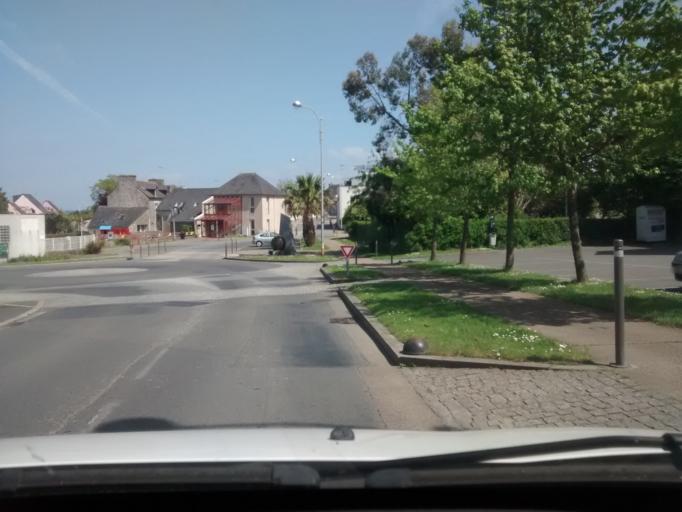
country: FR
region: Brittany
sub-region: Departement des Cotes-d'Armor
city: Langueux
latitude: 48.4958
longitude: -2.7170
